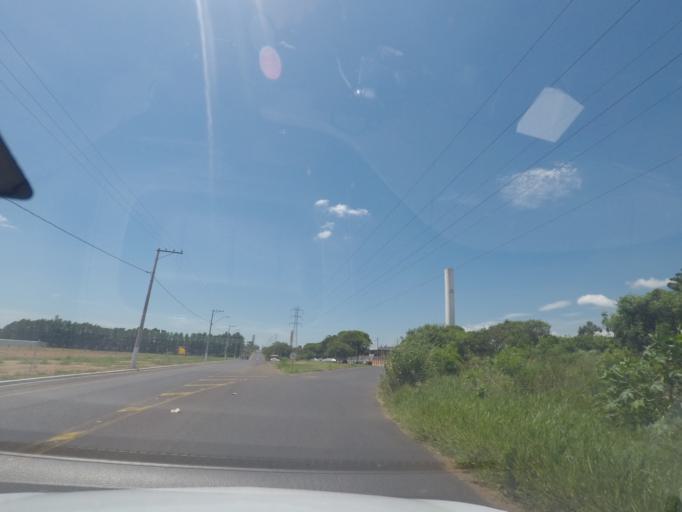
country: BR
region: Sao Paulo
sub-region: Matao
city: Matao
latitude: -21.6099
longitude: -48.3780
